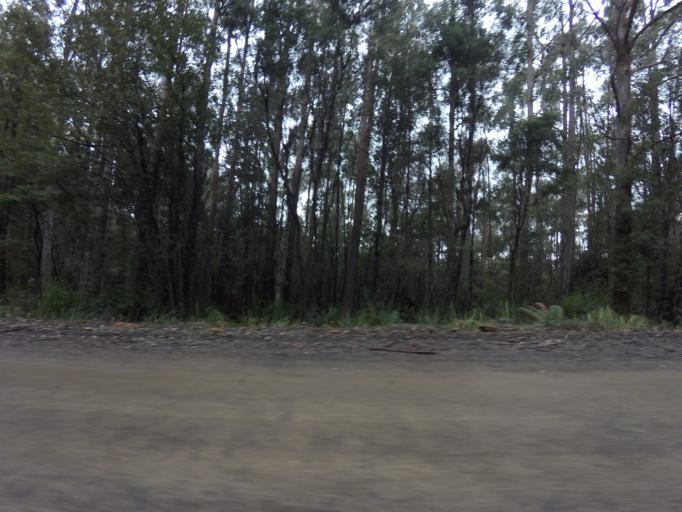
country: AU
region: Tasmania
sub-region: Huon Valley
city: Geeveston
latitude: -43.5266
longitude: 146.8843
